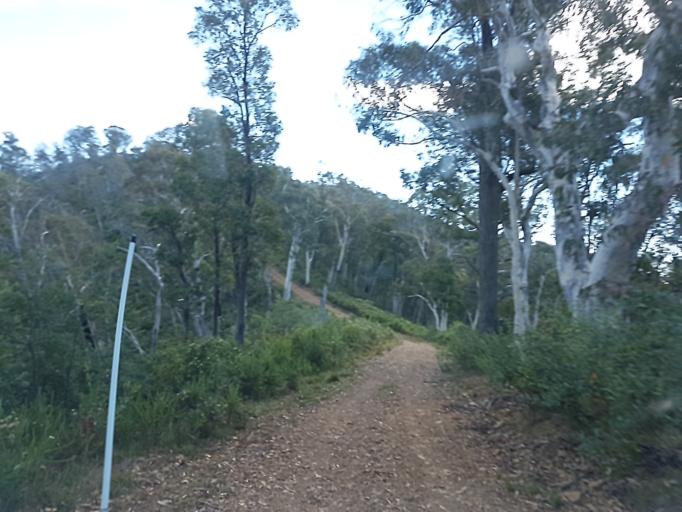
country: AU
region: Victoria
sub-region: Alpine
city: Mount Beauty
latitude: -36.9112
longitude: 147.0149
